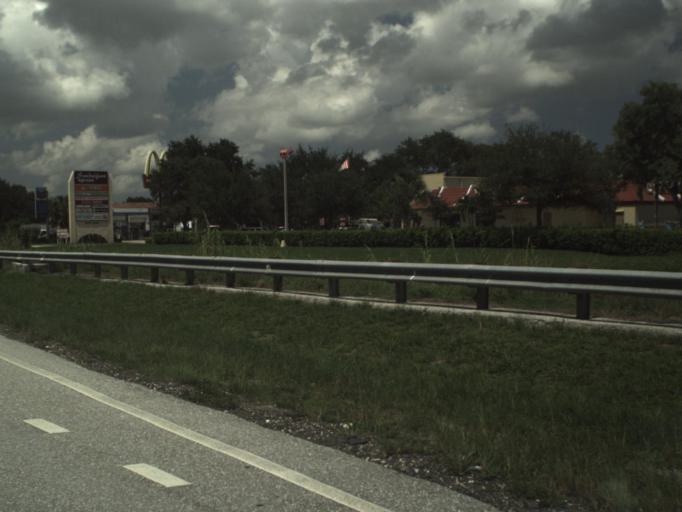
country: US
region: Florida
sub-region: Broward County
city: Parkland
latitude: 26.3321
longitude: -80.2029
